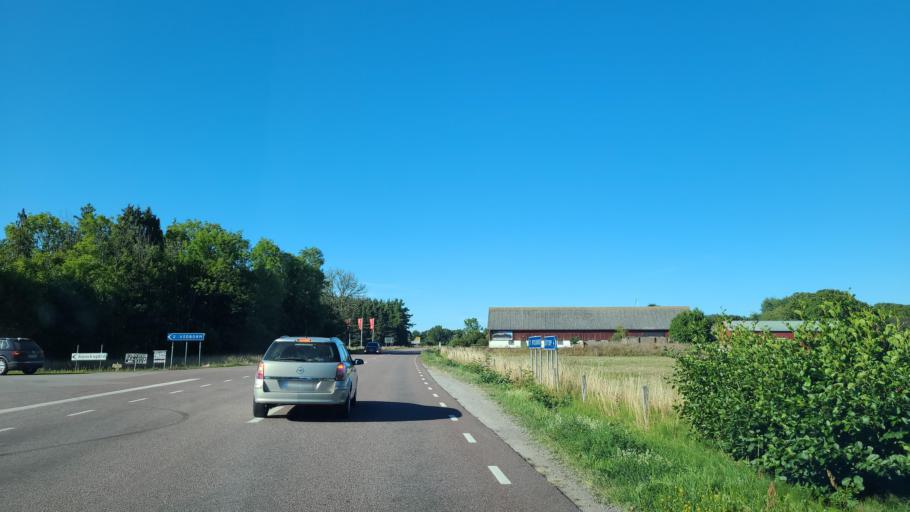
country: SE
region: Kalmar
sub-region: Borgholms Kommun
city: Borgholm
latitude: 57.1862
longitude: 17.0298
